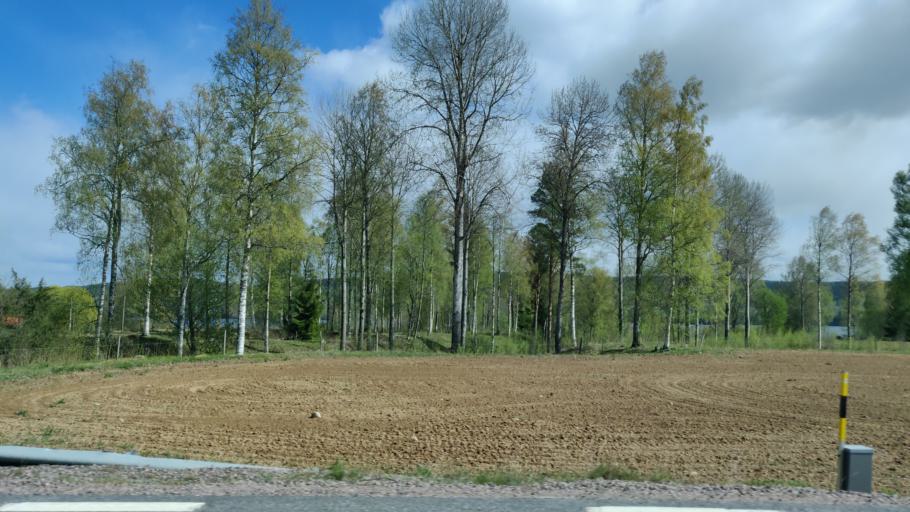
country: SE
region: Vaermland
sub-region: Munkfors Kommun
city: Munkfors
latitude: 59.8535
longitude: 13.7078
